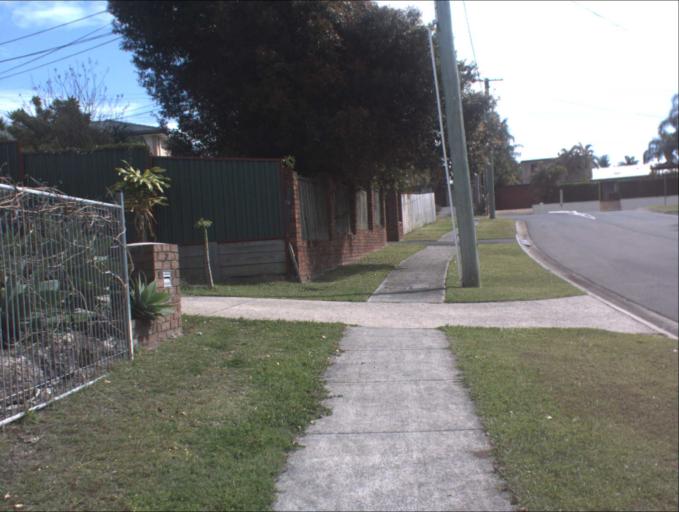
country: AU
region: Queensland
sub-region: Logan
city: Park Ridge South
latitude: -27.6717
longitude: 153.0382
